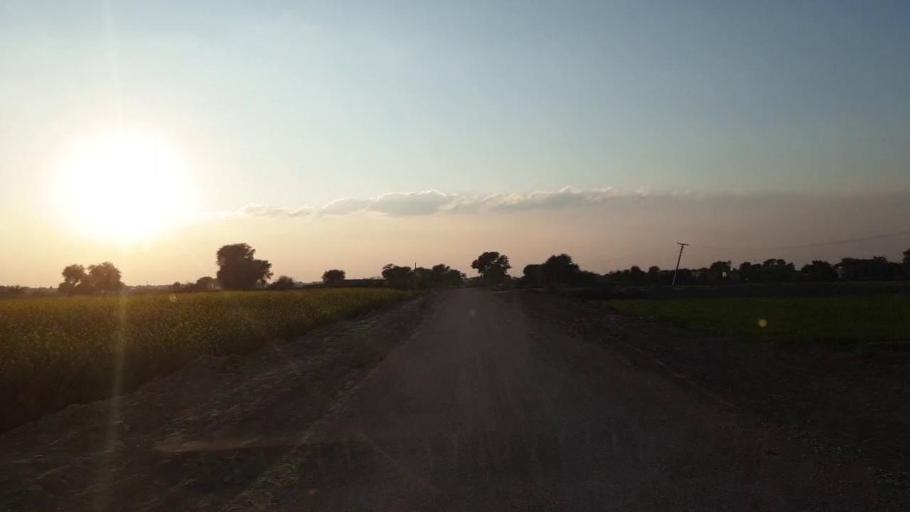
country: PK
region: Sindh
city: Shahpur Chakar
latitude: 26.1590
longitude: 68.5342
